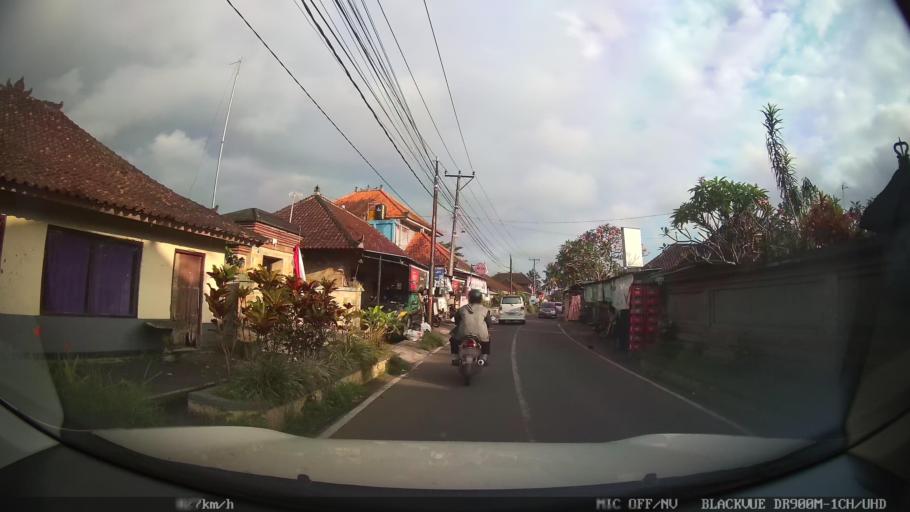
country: ID
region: Bali
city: Banjar Tebongkang
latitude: -8.5196
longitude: 115.2504
